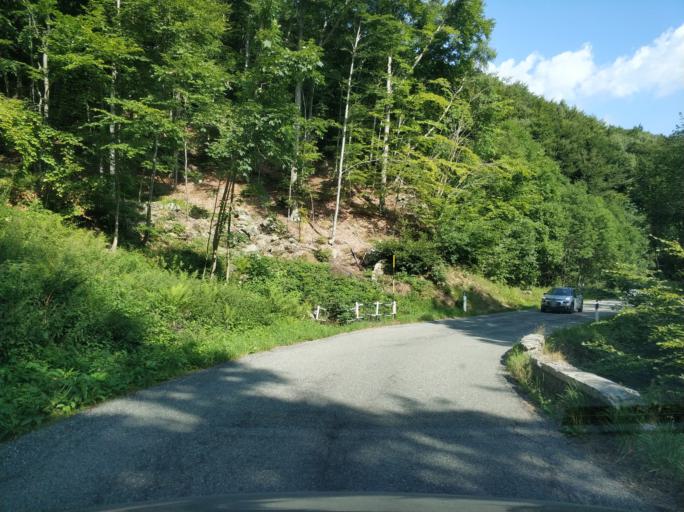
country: IT
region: Piedmont
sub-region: Provincia di Torino
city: Viu
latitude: 45.1870
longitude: 7.3655
